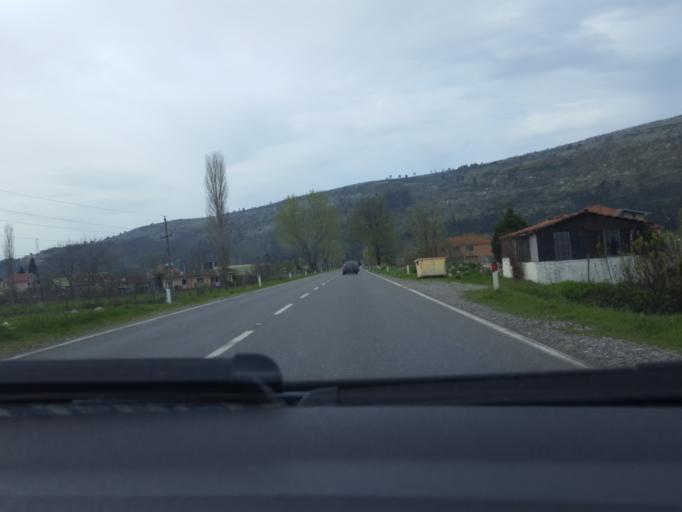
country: AL
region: Lezhe
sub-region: Rrethi i Lezhes
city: Balldreni i Ri
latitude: 41.8095
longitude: 19.6347
